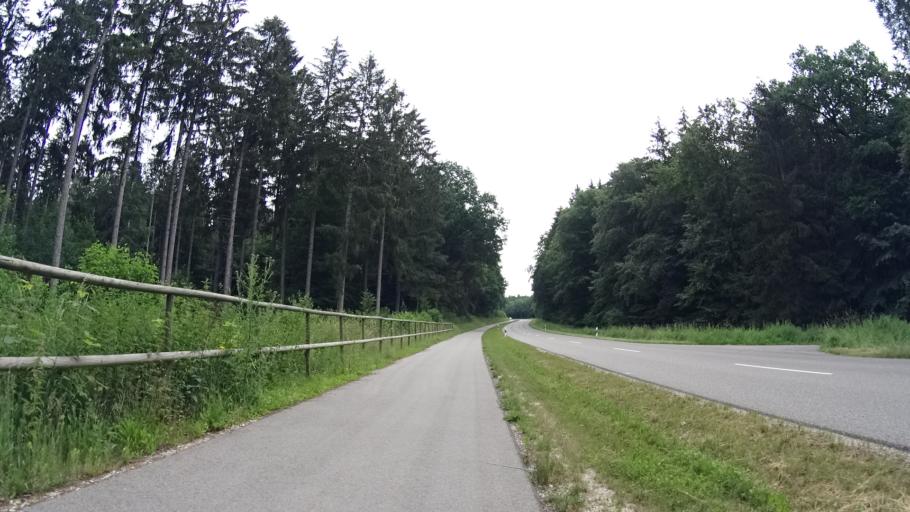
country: DE
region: Bavaria
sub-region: Upper Bavaria
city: Stammham
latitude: 48.8700
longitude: 11.4970
